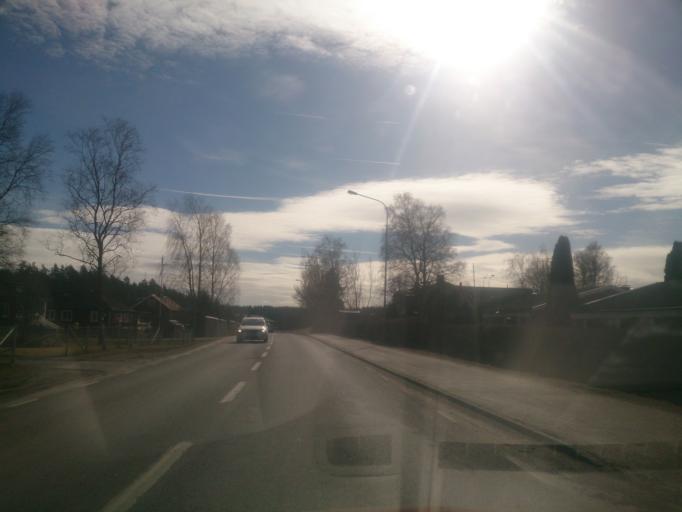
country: SE
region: OEstergoetland
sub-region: Finspangs Kommun
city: Finspang
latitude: 58.6869
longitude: 15.7508
